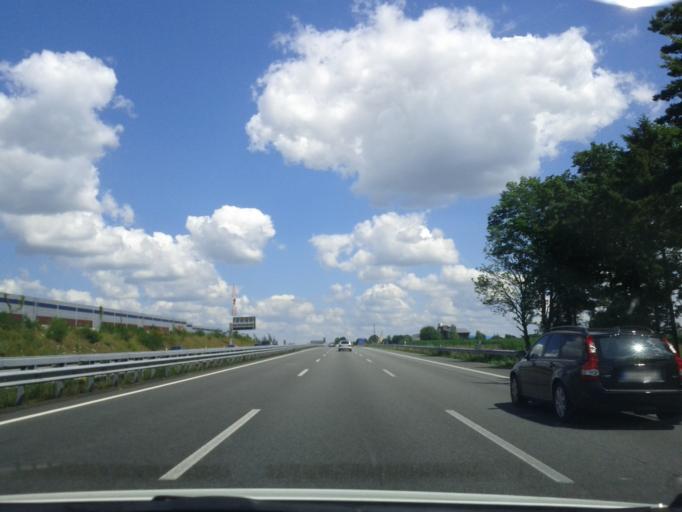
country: DE
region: Lower Saxony
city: Reessum
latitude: 53.1106
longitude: 9.2014
